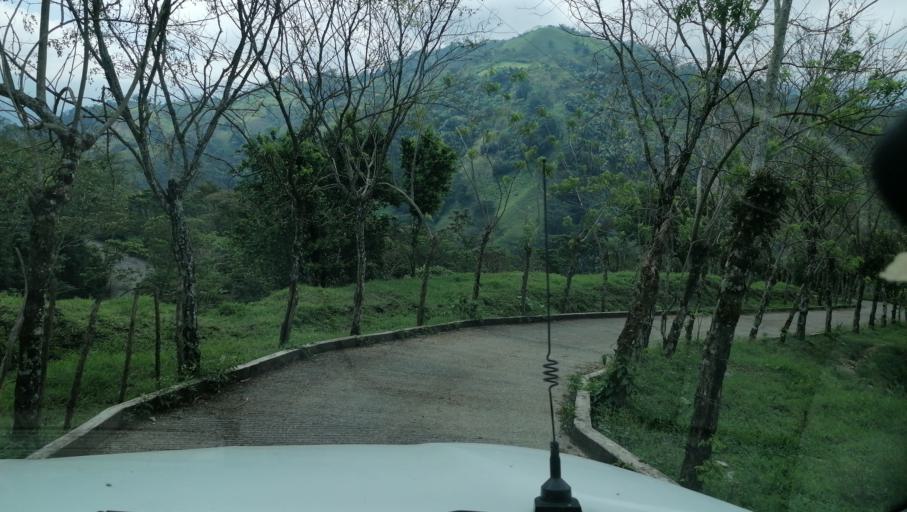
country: MX
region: Chiapas
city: Ixtacomitan
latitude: 17.3566
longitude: -93.1288
